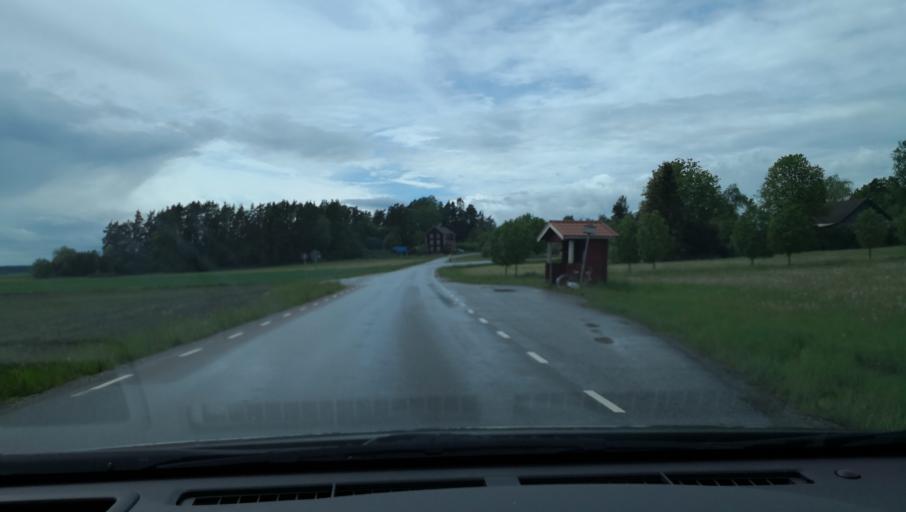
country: SE
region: Uppsala
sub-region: Enkopings Kommun
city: Orsundsbro
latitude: 59.6885
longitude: 17.3786
